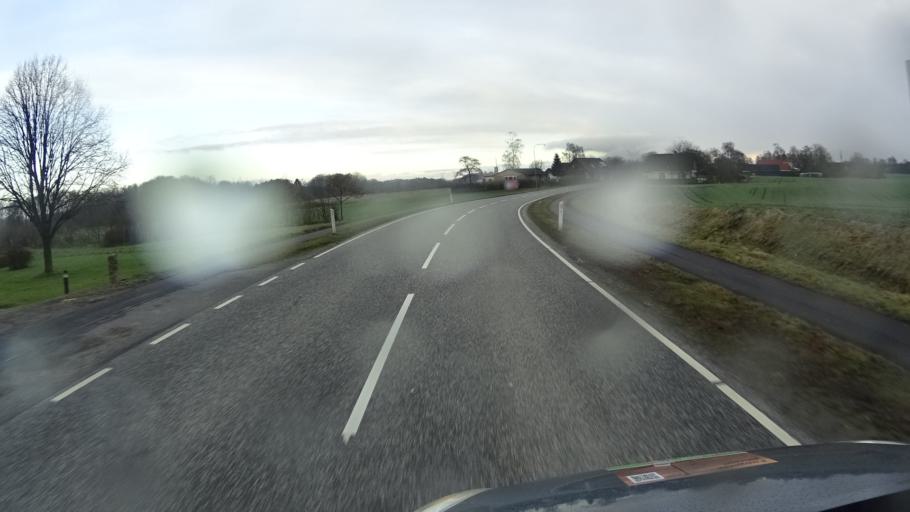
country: DK
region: South Denmark
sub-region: Vejle Kommune
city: Jelling
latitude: 55.7607
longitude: 9.4628
